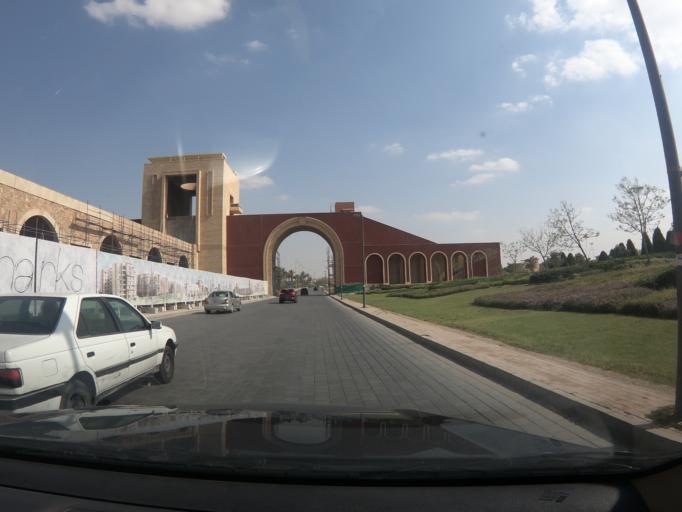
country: EG
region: Muhafazat al Qalyubiyah
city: Al Khankah
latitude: 30.1005
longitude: 31.6126
